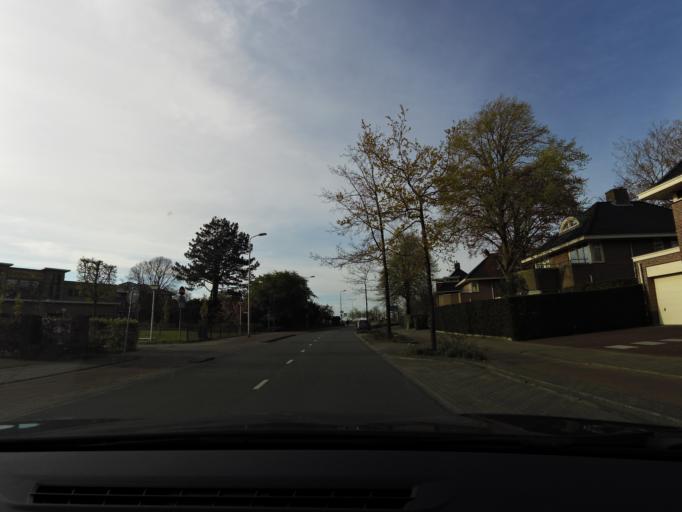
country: NL
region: South Holland
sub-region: Gemeente Lisse
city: Lisse
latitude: 52.2674
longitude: 4.5594
